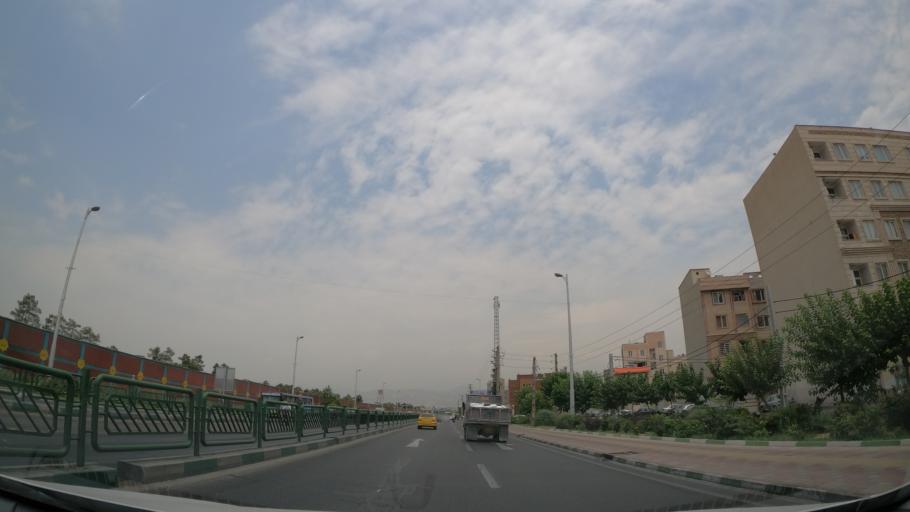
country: IR
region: Tehran
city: Tehran
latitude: 35.6857
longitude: 51.3417
